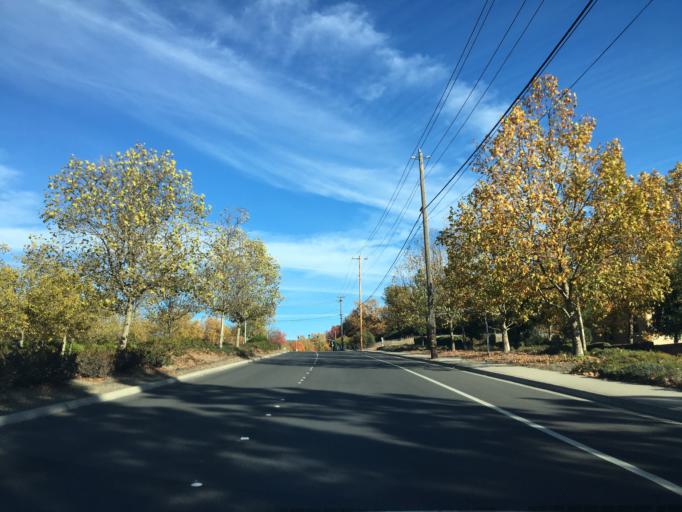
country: US
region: California
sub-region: Contra Costa County
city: Blackhawk
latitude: 37.7991
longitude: -121.9067
